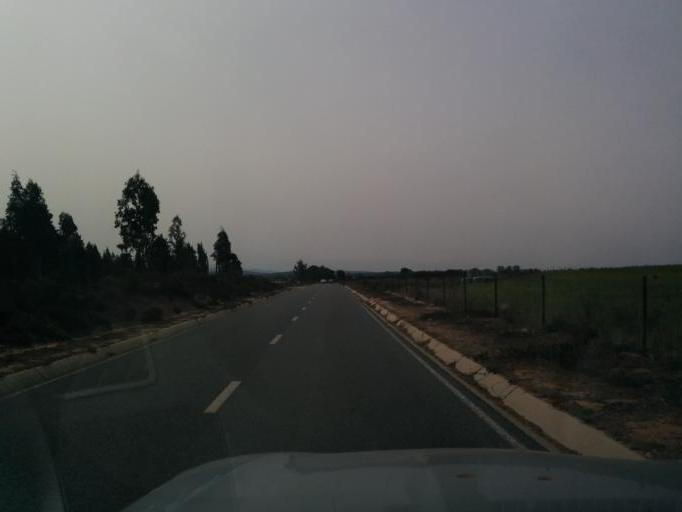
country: PT
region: Beja
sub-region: Odemira
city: Sao Teotonio
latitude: 37.5988
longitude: -8.7438
